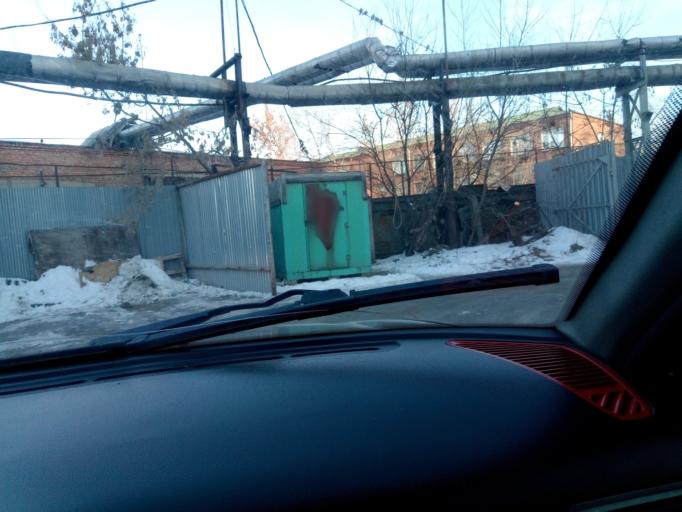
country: RU
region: Tula
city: Mendeleyevskiy
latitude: 54.1732
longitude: 37.5727
